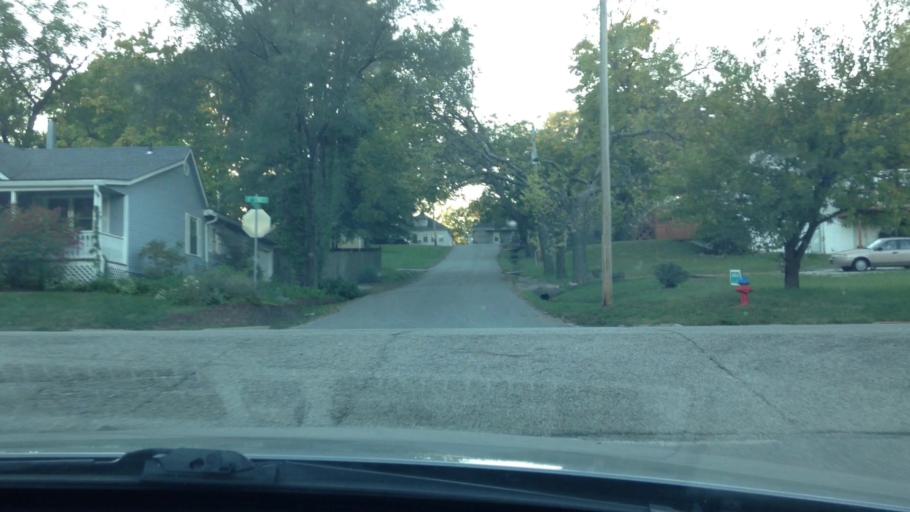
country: US
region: Kansas
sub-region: Leavenworth County
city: Leavenworth
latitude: 39.3129
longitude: -94.9281
